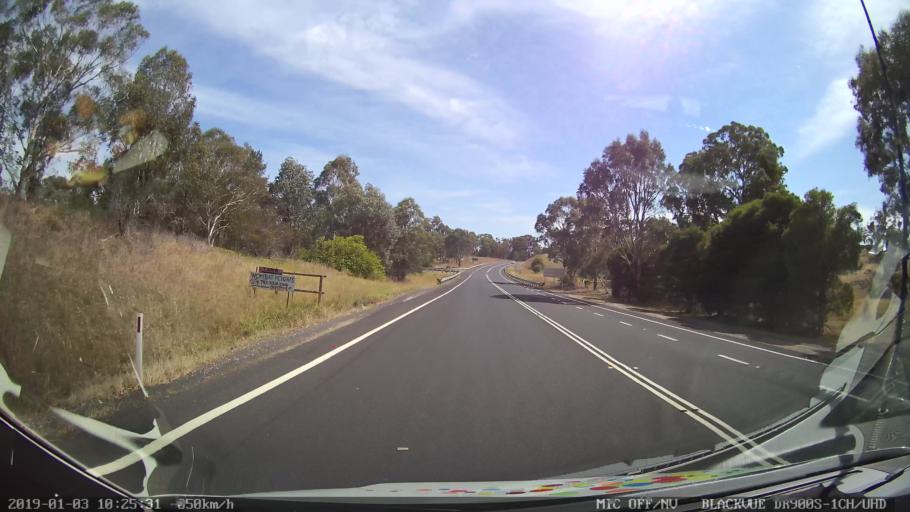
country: AU
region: New South Wales
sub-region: Young
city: Young
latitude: -34.4220
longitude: 148.2441
